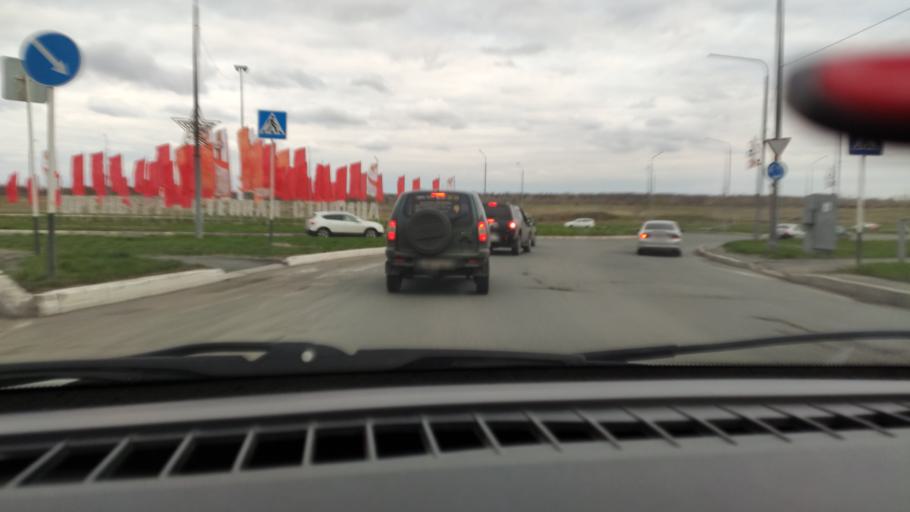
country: RU
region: Orenburg
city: Orenburg
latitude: 51.8108
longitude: 55.1794
